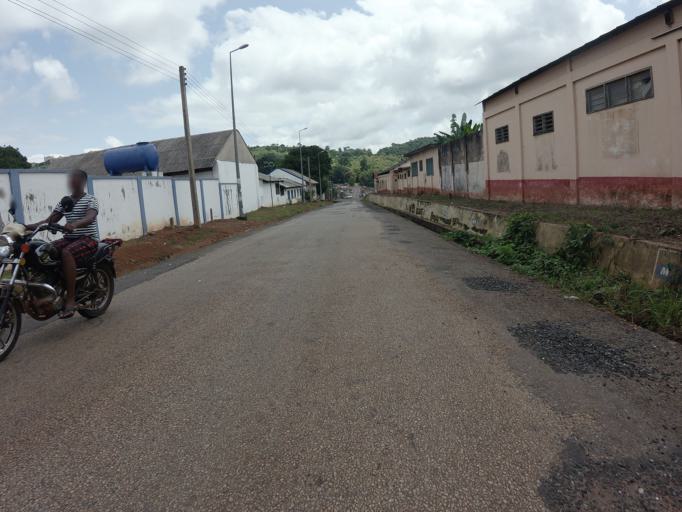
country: GH
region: Volta
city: Ho
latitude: 6.6099
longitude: 0.4605
